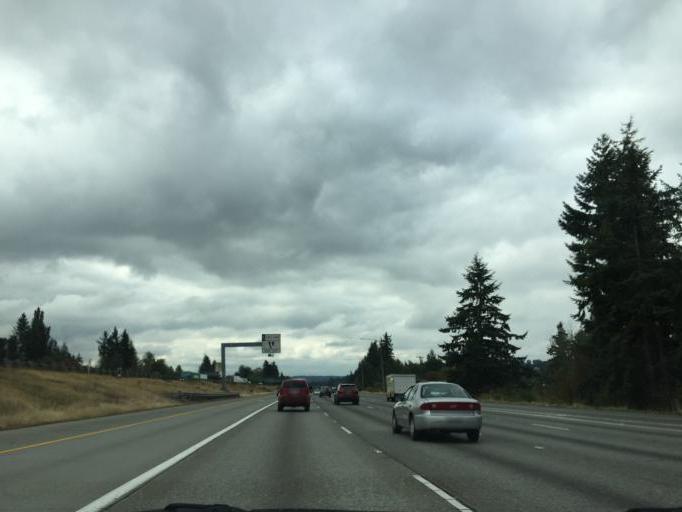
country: US
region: Washington
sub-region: Pierce County
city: Milton
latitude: 47.2704
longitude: -122.3170
